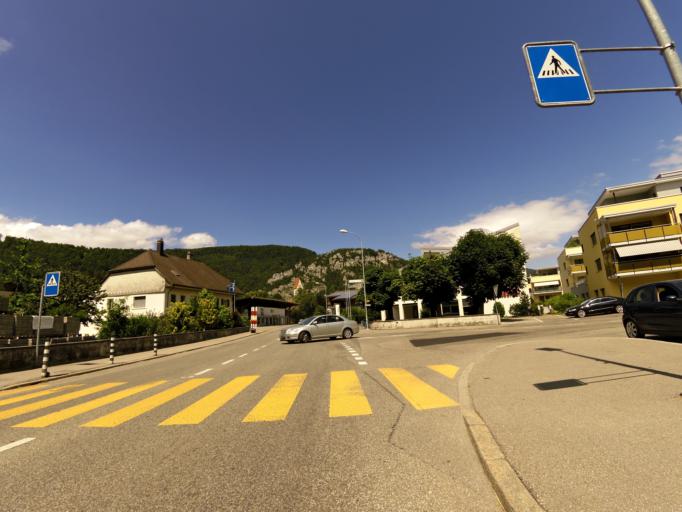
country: CH
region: Solothurn
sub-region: Bezirk Thal
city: Balsthal
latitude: 47.3140
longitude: 7.6930
